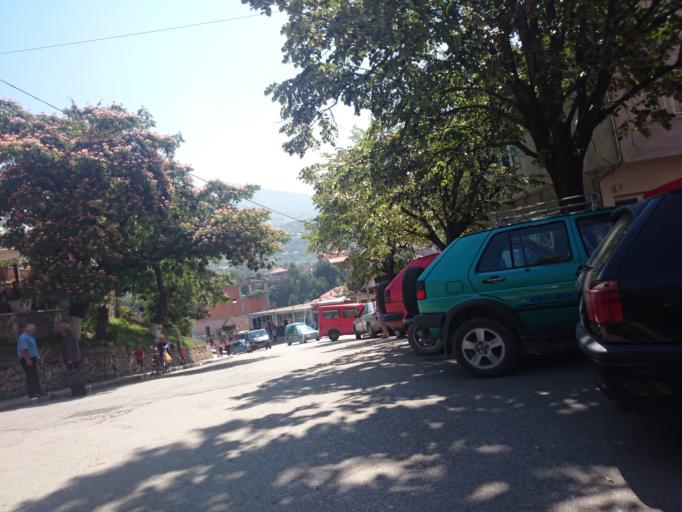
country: AL
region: Diber
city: Peshkopi
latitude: 41.6843
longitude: 20.4316
